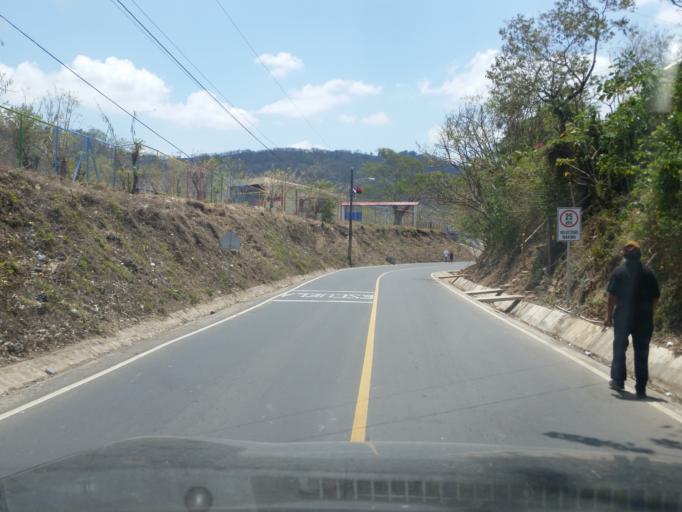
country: NI
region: Boaco
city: Boaco
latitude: 12.4753
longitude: -85.6453
